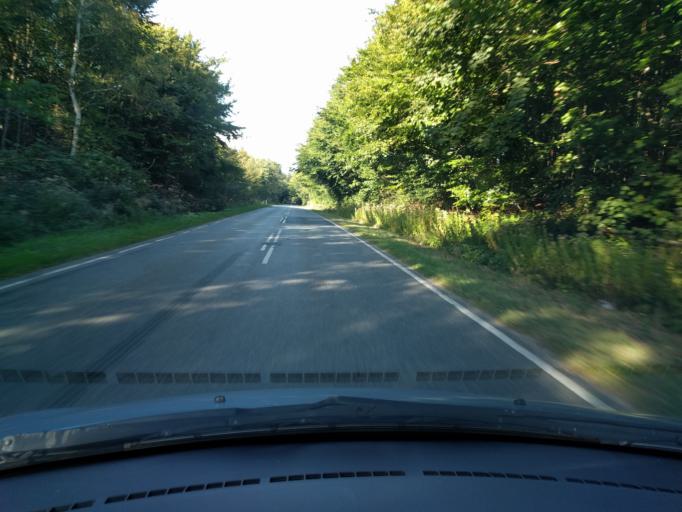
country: DK
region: South Denmark
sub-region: Assens Kommune
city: Assens
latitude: 55.2190
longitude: 9.9974
